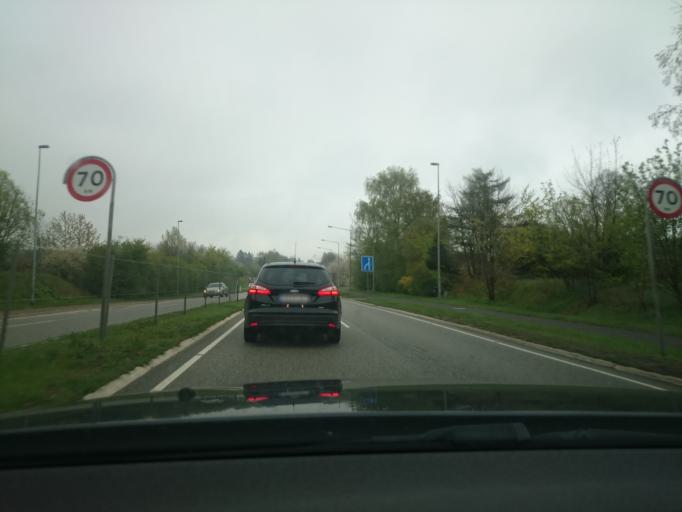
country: DK
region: Capital Region
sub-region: Herlev Kommune
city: Herlev
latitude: 55.7513
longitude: 12.4043
